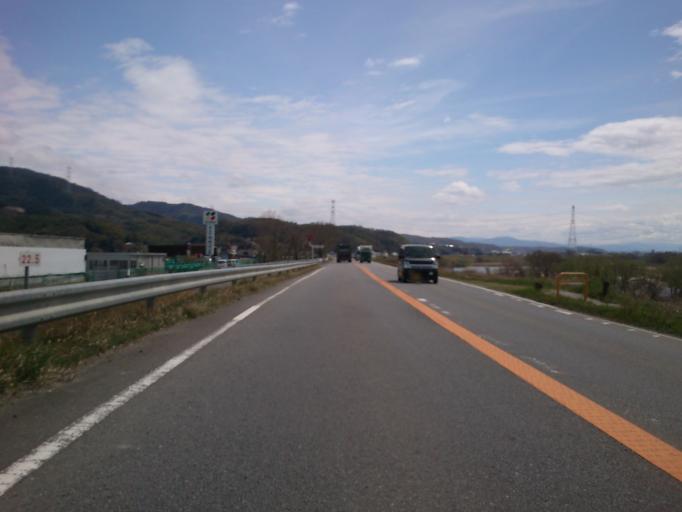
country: JP
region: Kyoto
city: Tanabe
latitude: 34.8162
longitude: 135.8007
